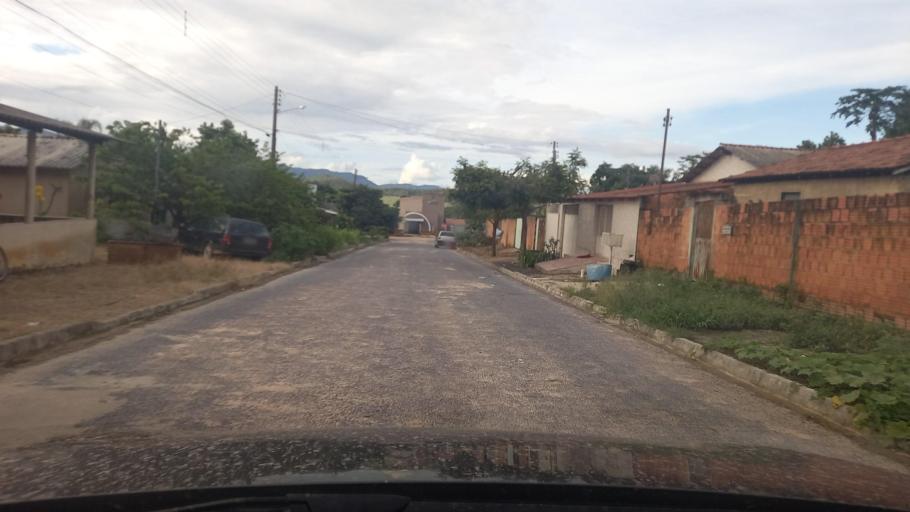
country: BR
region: Goias
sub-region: Cavalcante
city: Cavalcante
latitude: -13.7983
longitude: -47.4480
